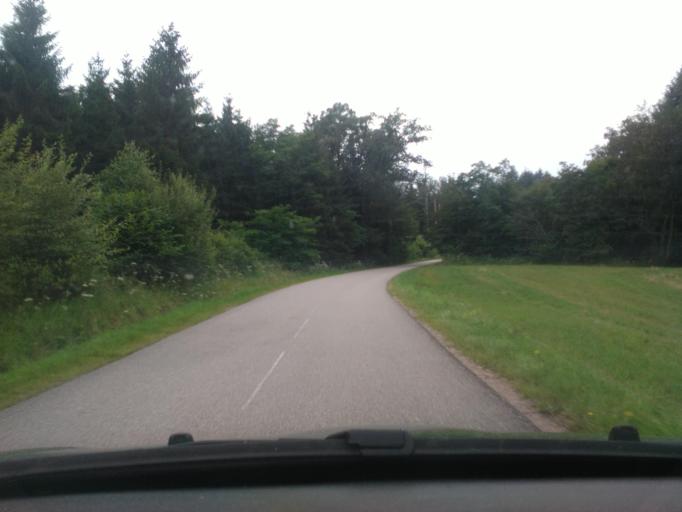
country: FR
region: Lorraine
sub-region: Departement des Vosges
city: Bruyeres
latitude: 48.2116
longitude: 6.7486
